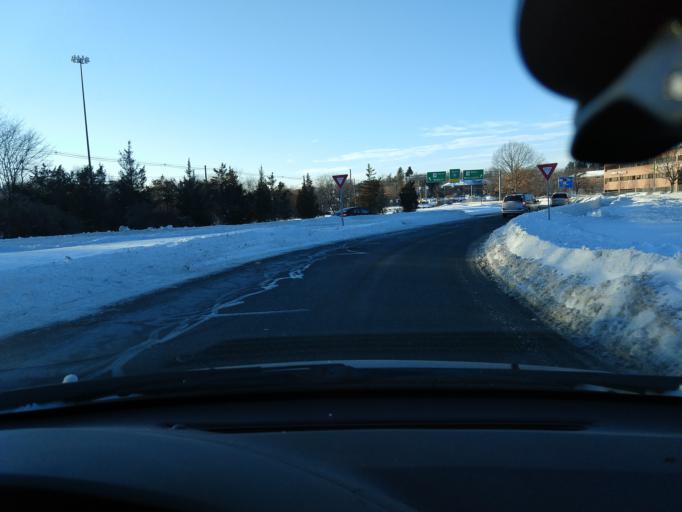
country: US
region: Massachusetts
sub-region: Middlesex County
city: Woburn
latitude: 42.5002
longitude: -71.1560
